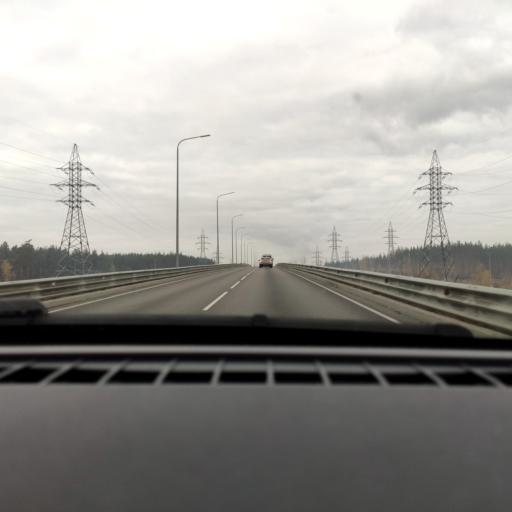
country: RU
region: Voronezj
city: Somovo
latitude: 51.7266
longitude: 39.3143
